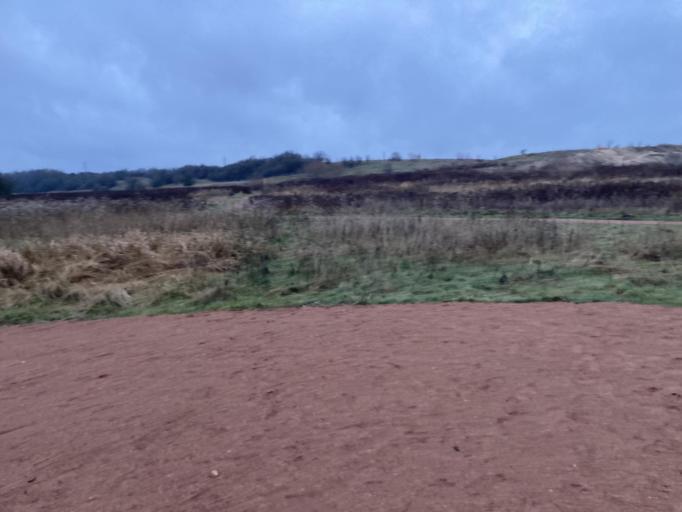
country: DK
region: Capital Region
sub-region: Hoje-Taastrup Kommune
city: Flong
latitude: 55.6771
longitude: 12.2396
